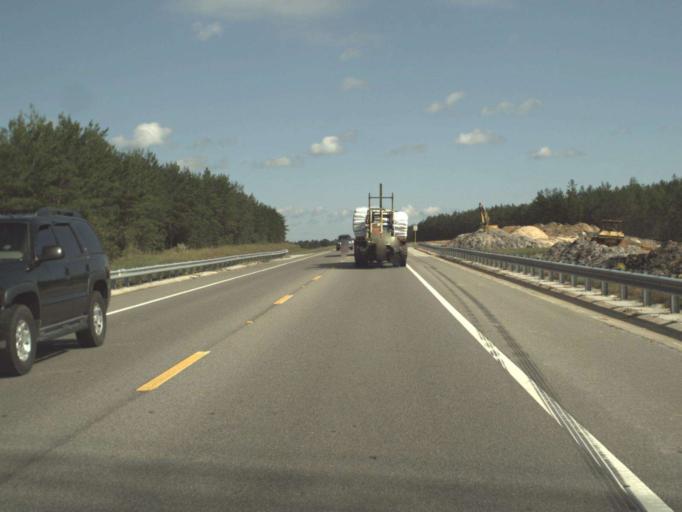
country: US
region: Florida
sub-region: Walton County
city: Freeport
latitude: 30.5156
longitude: -86.1107
